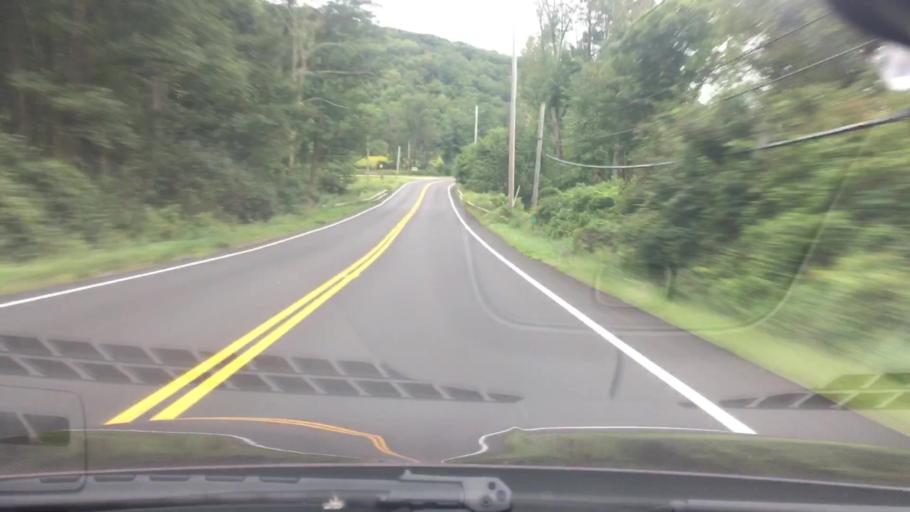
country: US
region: New York
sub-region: Dutchess County
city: Dover Plains
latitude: 41.8436
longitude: -73.5922
